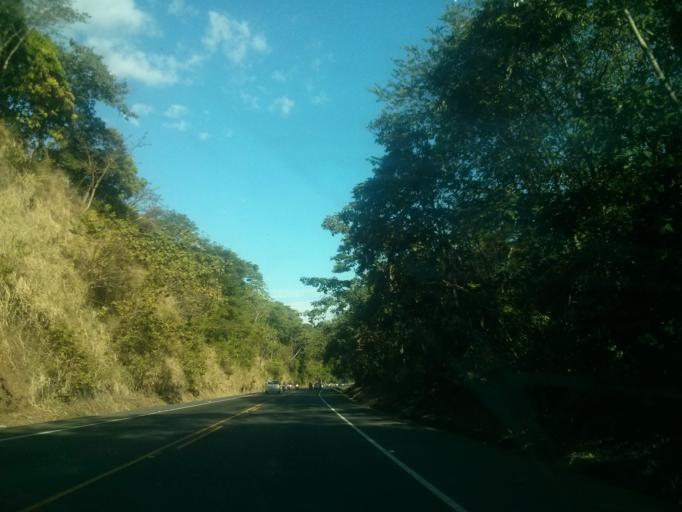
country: CR
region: Alajuela
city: Orotina
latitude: 9.9002
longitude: -84.5519
